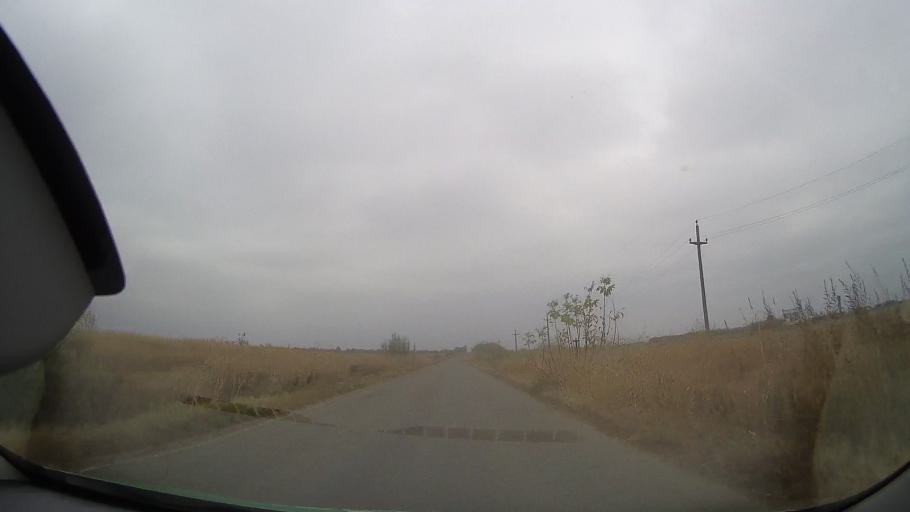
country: RO
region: Buzau
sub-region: Comuna Glodeanu-Silistea
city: Glodeanu-Silistea
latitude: 44.8161
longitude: 26.8442
